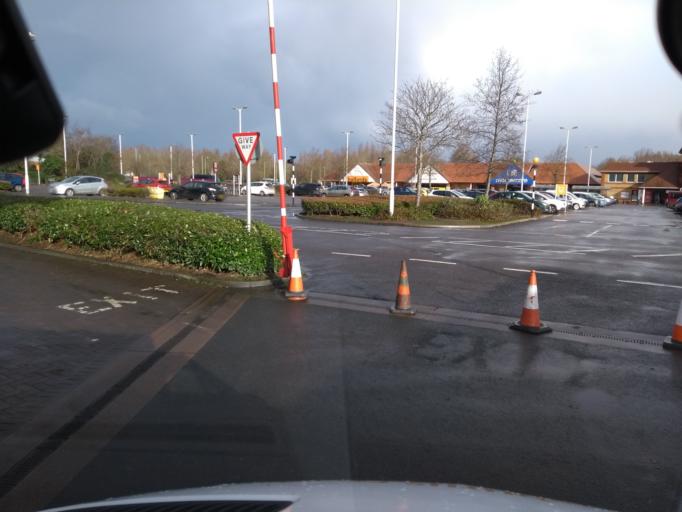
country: GB
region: England
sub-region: Somerset
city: Creech Saint Michael
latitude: 51.0207
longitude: -3.0629
